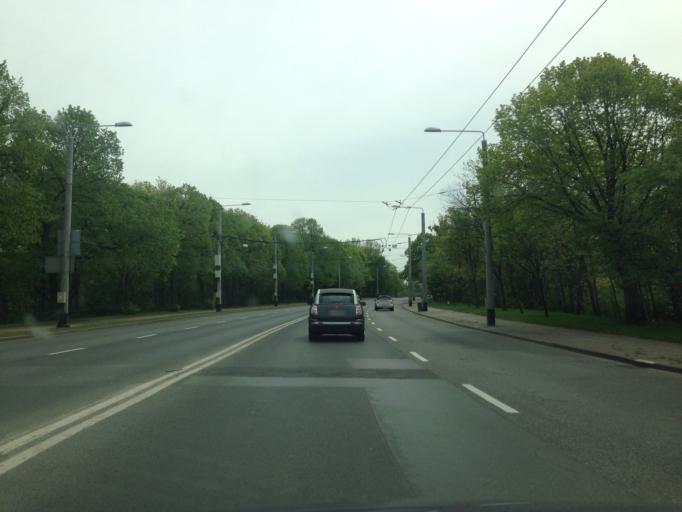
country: PL
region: Pomeranian Voivodeship
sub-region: Sopot
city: Sopot
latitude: 54.4561
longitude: 18.5559
